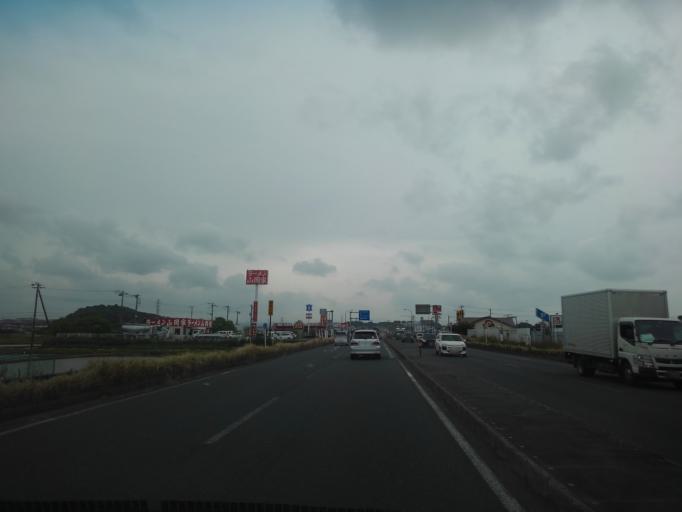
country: JP
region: Chiba
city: Kisarazu
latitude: 35.3963
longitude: 139.9413
